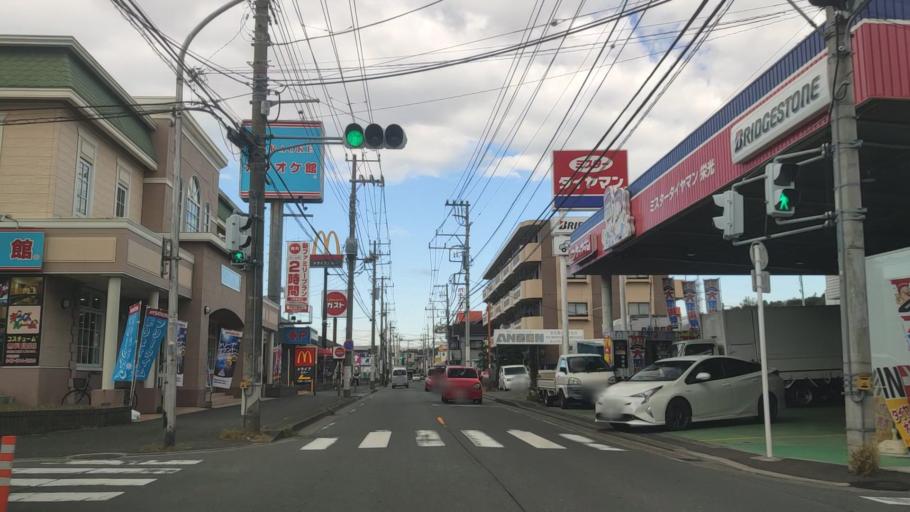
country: JP
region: Kanagawa
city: Minami-rinkan
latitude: 35.4233
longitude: 139.5317
